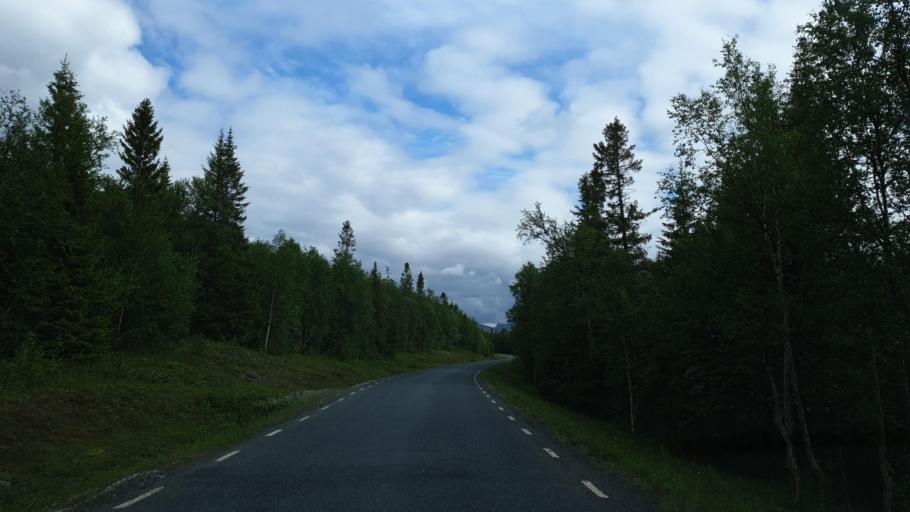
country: SE
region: Vaesterbotten
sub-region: Vilhelmina Kommun
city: Sjoberg
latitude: 65.2852
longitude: 15.2953
